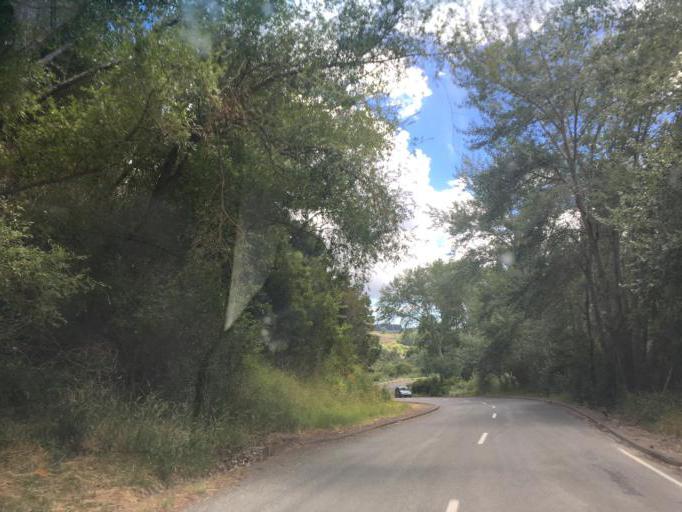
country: NZ
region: Hawke's Bay
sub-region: Hastings District
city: Hastings
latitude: -39.7363
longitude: 176.8983
